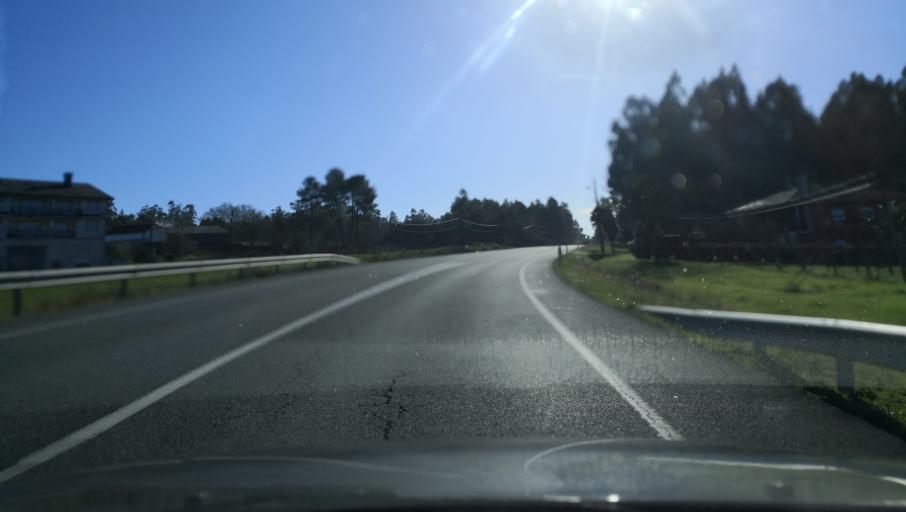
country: ES
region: Galicia
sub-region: Provincia da Coruna
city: Vedra
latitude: 42.7949
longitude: -8.4633
